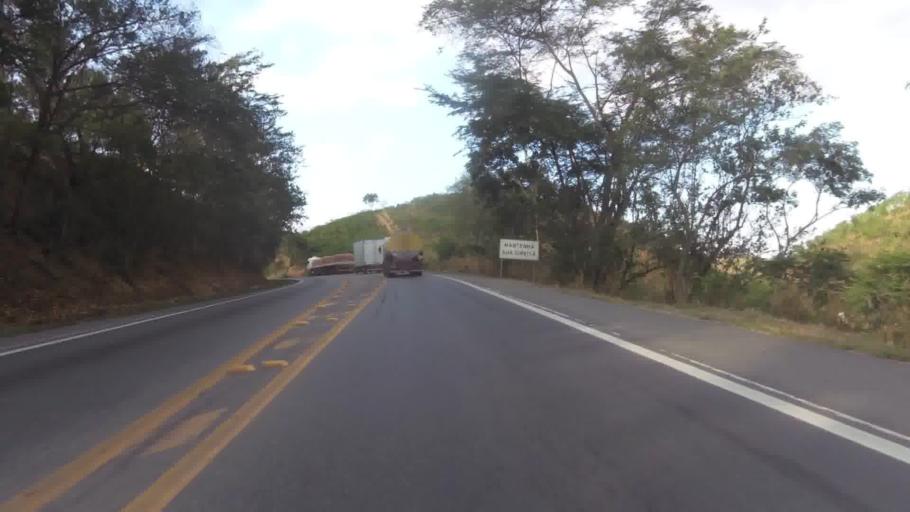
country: BR
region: Espirito Santo
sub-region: Rio Novo Do Sul
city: Rio Novo do Sul
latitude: -20.8870
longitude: -40.9831
